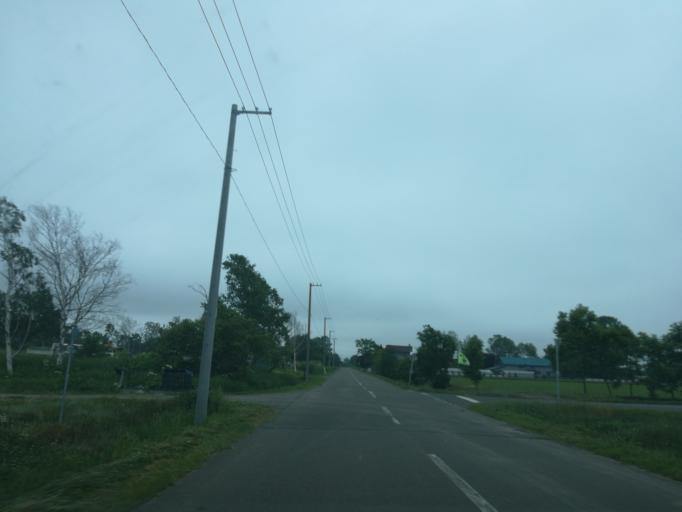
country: JP
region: Hokkaido
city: Ebetsu
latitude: 43.0695
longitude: 141.6408
